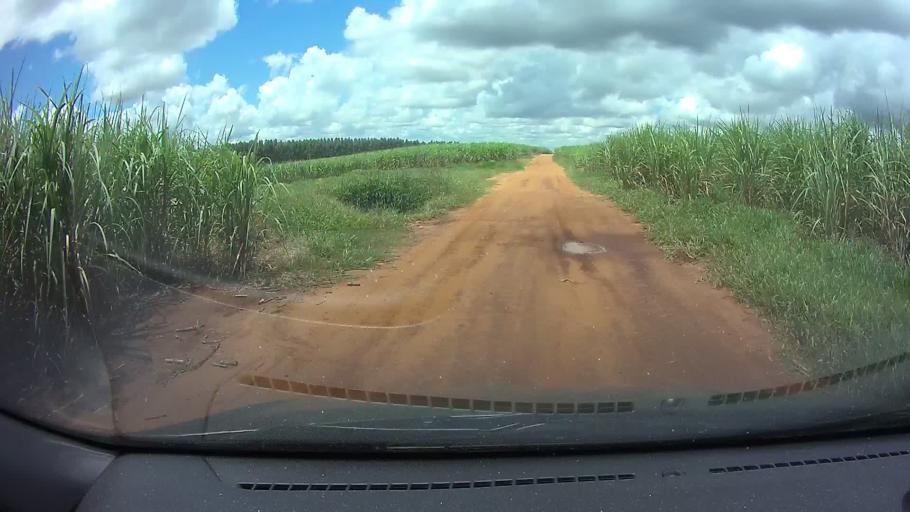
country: PY
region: Paraguari
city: La Colmena
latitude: -25.9646
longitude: -56.7595
